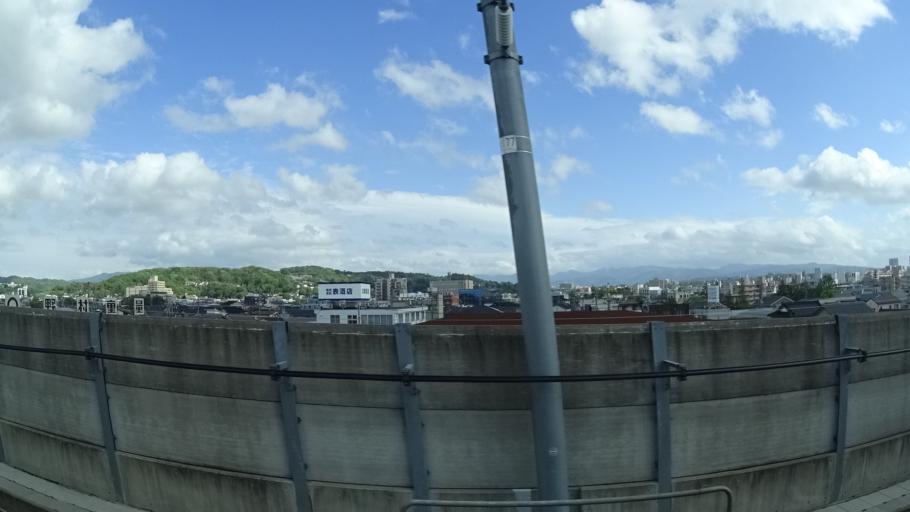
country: JP
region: Ishikawa
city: Kanazawa-shi
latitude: 36.5862
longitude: 136.6609
